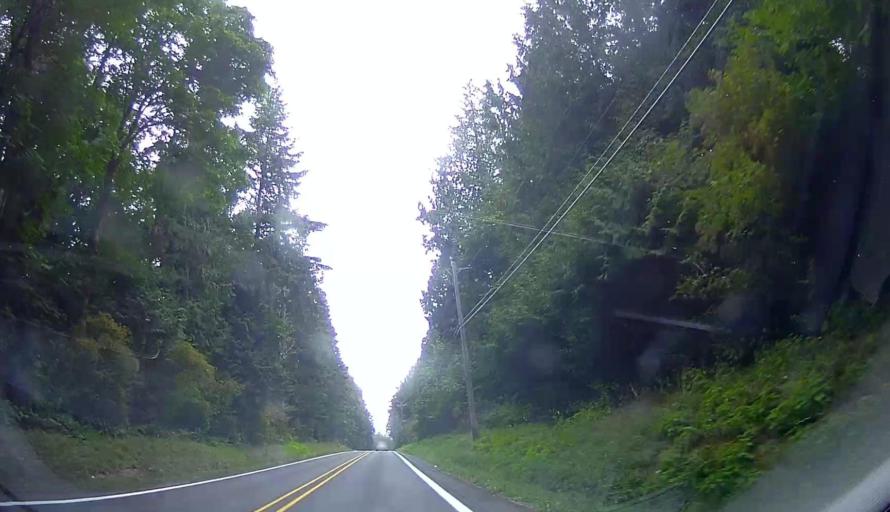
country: US
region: Washington
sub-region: Snohomish County
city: Warm Beach
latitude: 48.1205
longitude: -122.3521
